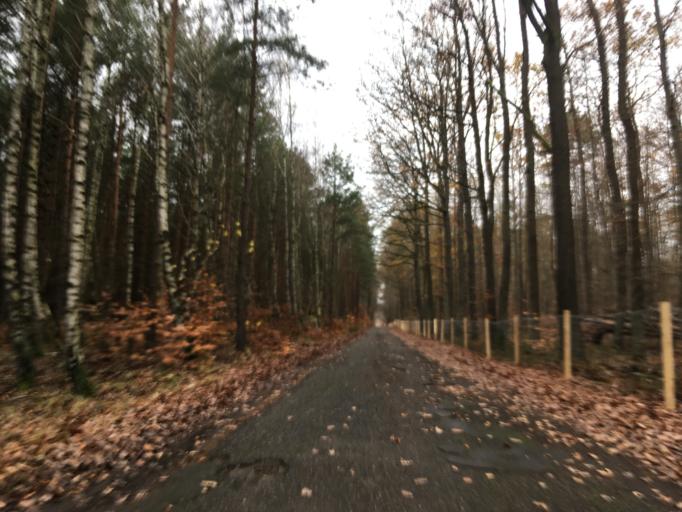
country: DE
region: Brandenburg
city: Jamlitz
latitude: 52.0747
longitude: 14.4798
